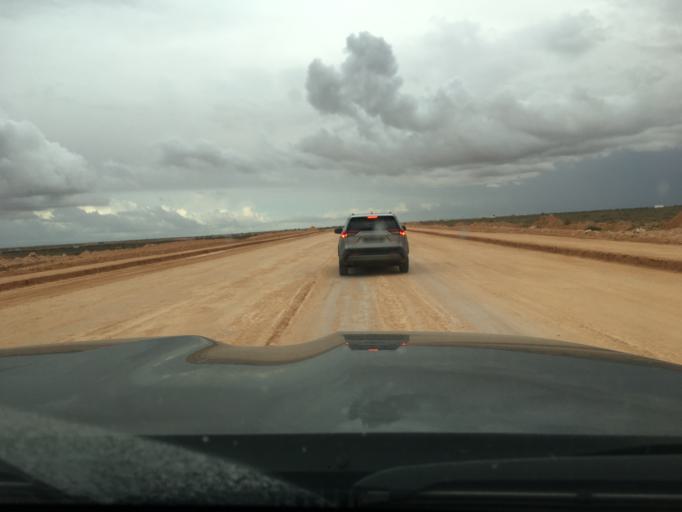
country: TN
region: Madanin
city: Medenine
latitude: 33.2792
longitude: 10.5936
